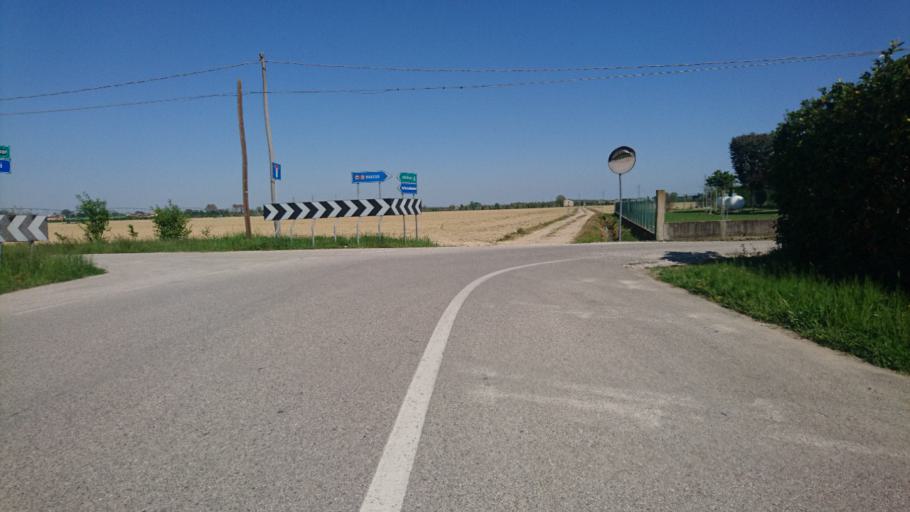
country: IT
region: Veneto
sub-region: Provincia di Venezia
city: Marcon-Gaggio-Colmello
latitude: 45.5737
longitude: 12.2872
